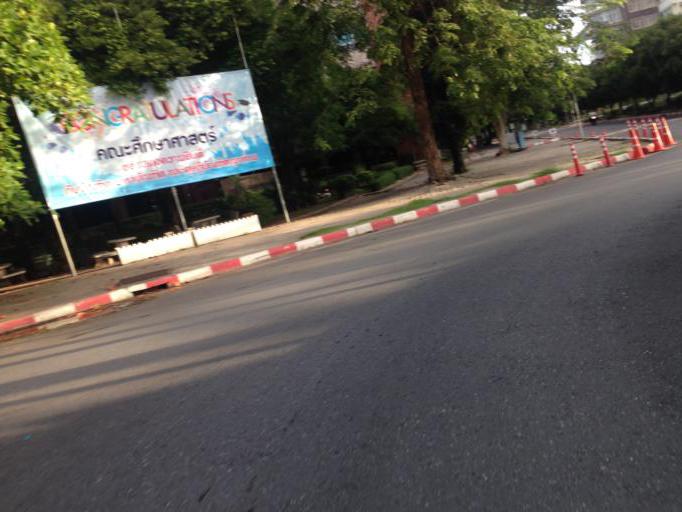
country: TH
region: Chon Buri
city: Chon Buri
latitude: 13.2787
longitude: 100.9246
